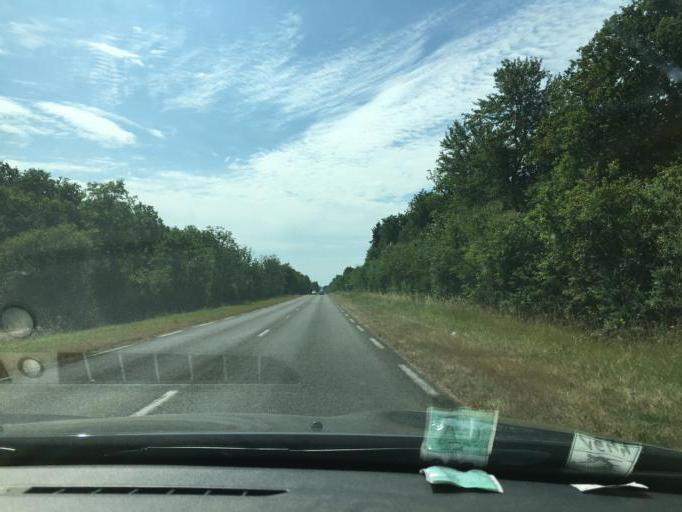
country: FR
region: Centre
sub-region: Departement du Loiret
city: La Ferte-Saint-Aubin
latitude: 47.7015
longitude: 1.9477
